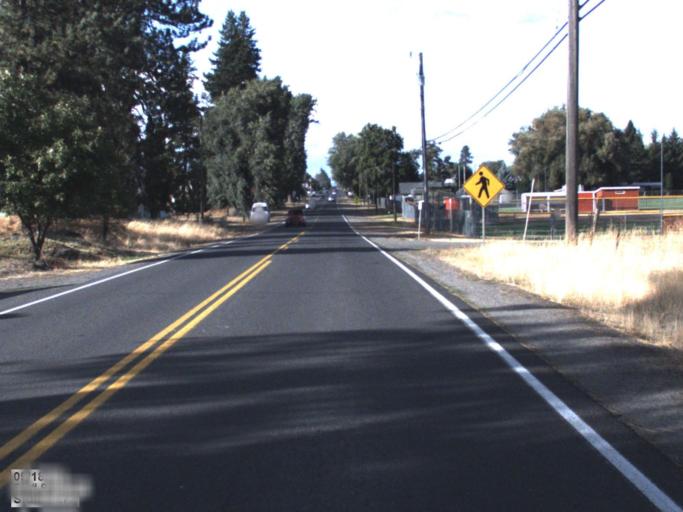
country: US
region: Washington
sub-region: Spokane County
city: Medical Lake
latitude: 47.5681
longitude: -117.6826
